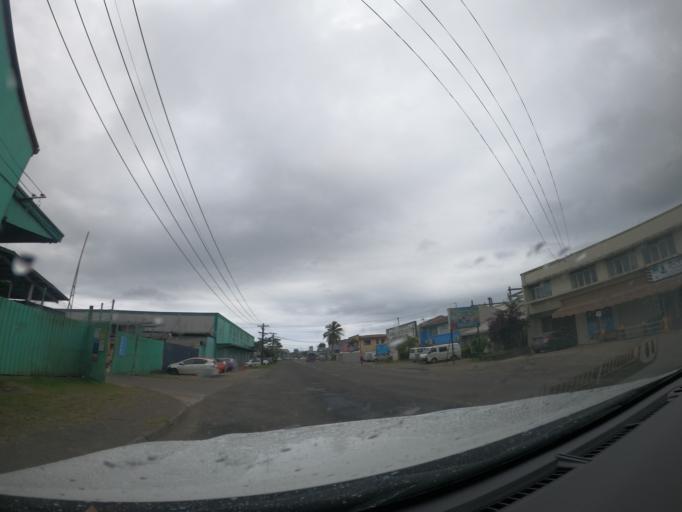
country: FJ
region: Central
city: Suva
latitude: -18.1263
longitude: 178.4313
